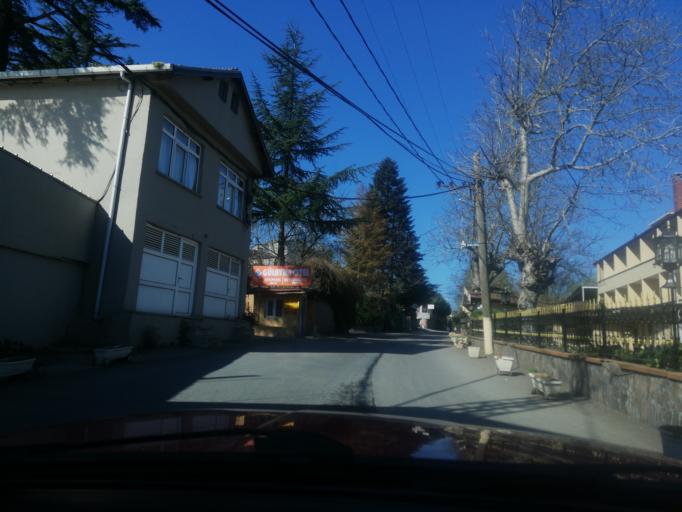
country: TR
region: Istanbul
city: Mahmut Sevket Pasa
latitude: 41.1117
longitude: 29.2110
